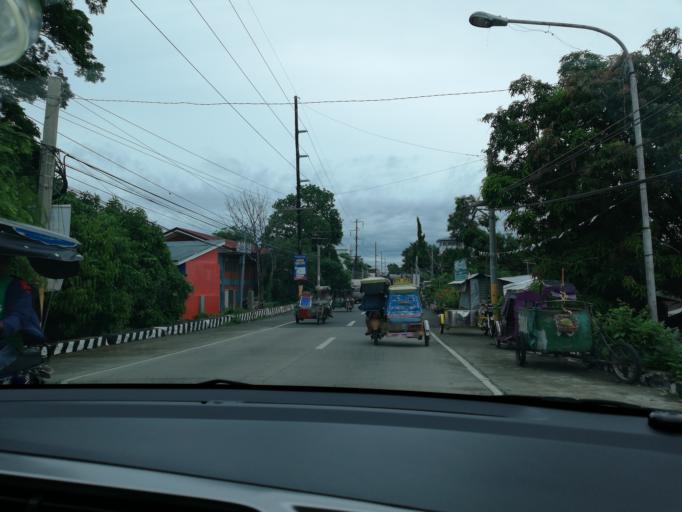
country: PH
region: Ilocos
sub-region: Province of Ilocos Sur
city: Vigan
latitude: 17.5786
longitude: 120.3862
